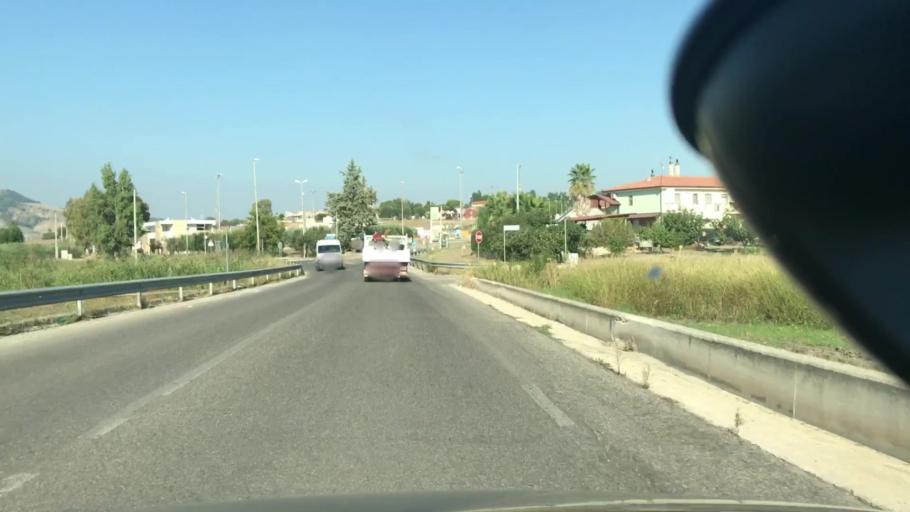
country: IT
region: Basilicate
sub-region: Provincia di Matera
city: La Martella
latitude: 40.6588
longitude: 16.5421
